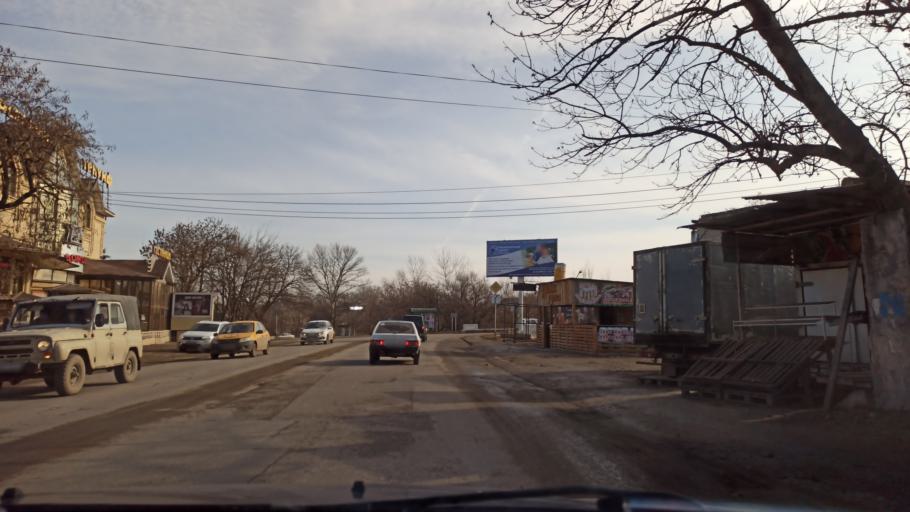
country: RU
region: Stavropol'skiy
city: Yessentuki
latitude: 44.0292
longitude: 42.8585
